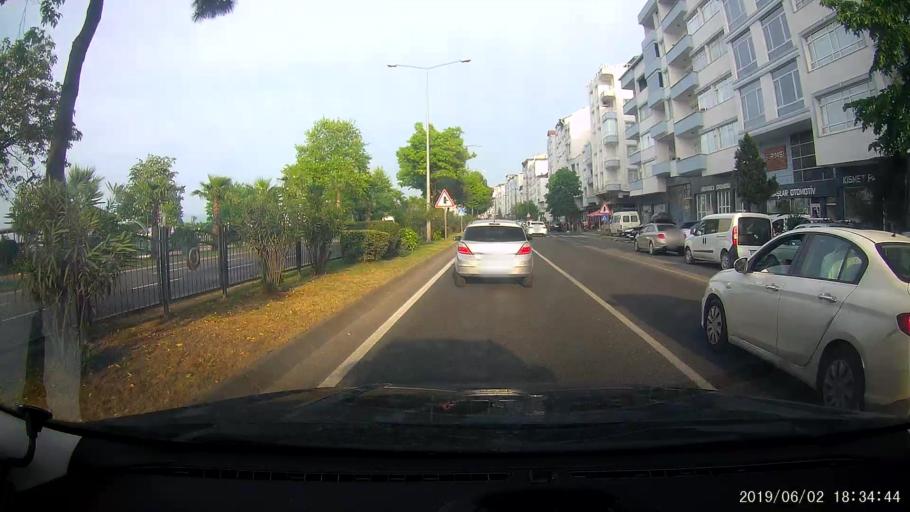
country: TR
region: Ordu
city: Fatsa
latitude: 41.0283
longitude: 37.5074
